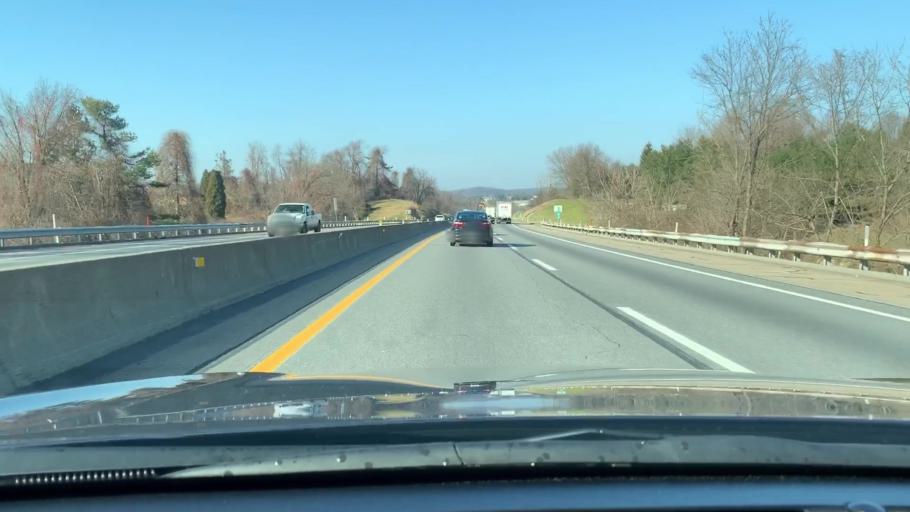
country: US
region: Pennsylvania
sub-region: Chester County
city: Downingtown
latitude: 40.0760
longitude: -75.6982
